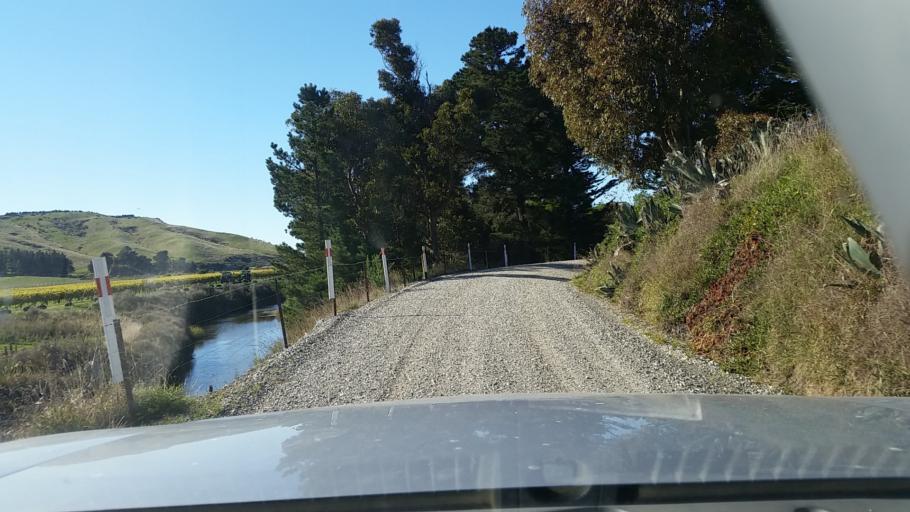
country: NZ
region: Marlborough
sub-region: Marlborough District
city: Blenheim
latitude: -41.6667
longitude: 174.1510
